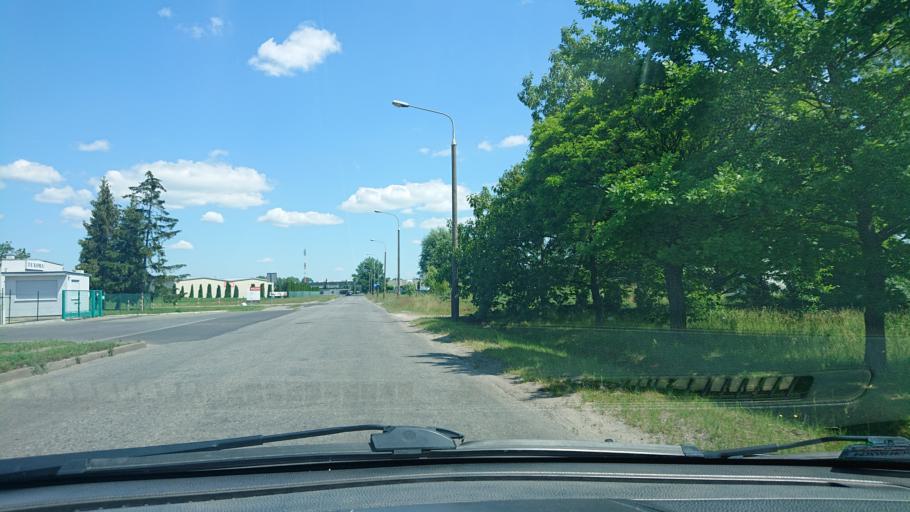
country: PL
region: Greater Poland Voivodeship
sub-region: Powiat gnieznienski
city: Gniezno
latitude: 52.5245
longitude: 17.6150
